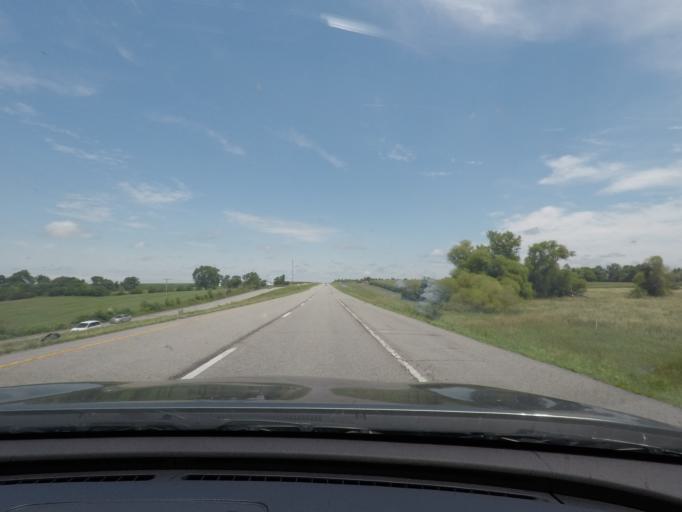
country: US
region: Missouri
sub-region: Saline County
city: Marshall
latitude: 39.0254
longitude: -93.1953
